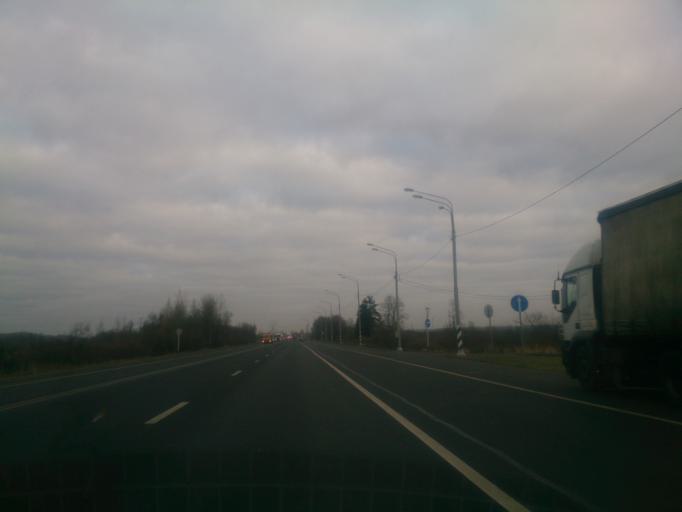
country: RU
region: Novgorod
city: Chudovo
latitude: 58.9076
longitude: 31.5031
